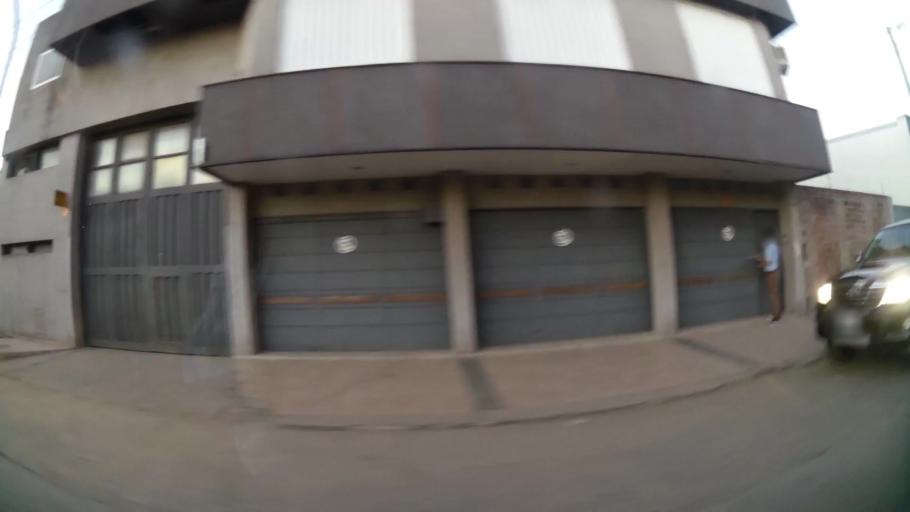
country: AR
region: Santa Fe
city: Santa Fe de la Vera Cruz
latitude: -31.6019
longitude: -60.7107
